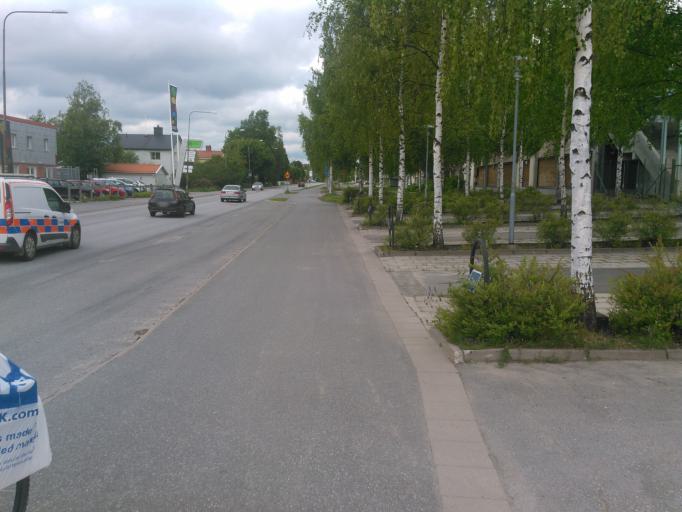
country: SE
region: Vaesterbotten
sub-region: Umea Kommun
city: Umea
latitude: 63.8292
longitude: 20.2842
